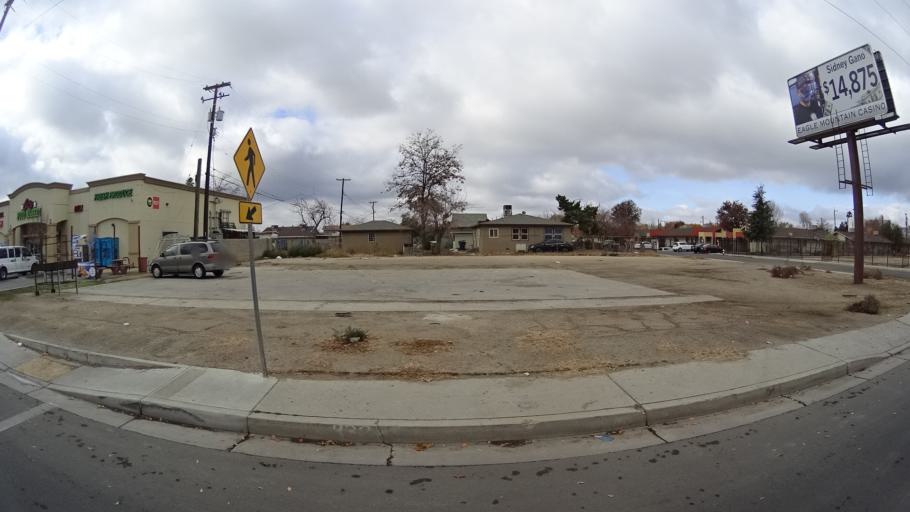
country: US
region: California
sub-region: Kern County
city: Bakersfield
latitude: 35.3663
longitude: -118.9852
